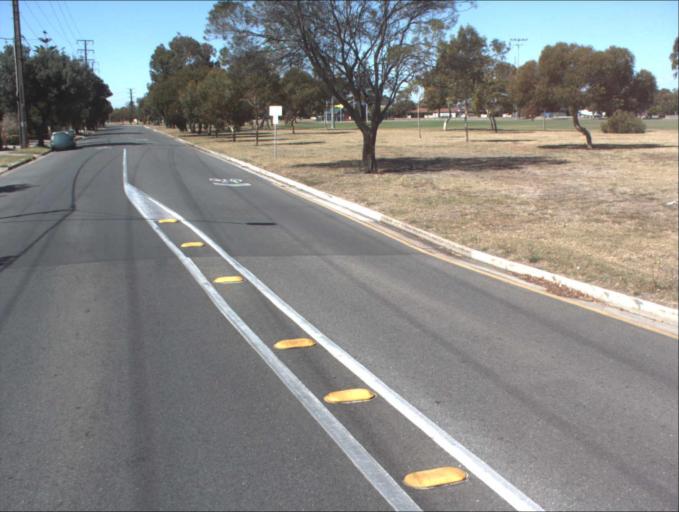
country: AU
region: South Australia
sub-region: Port Adelaide Enfield
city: Birkenhead
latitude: -34.8183
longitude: 138.4981
